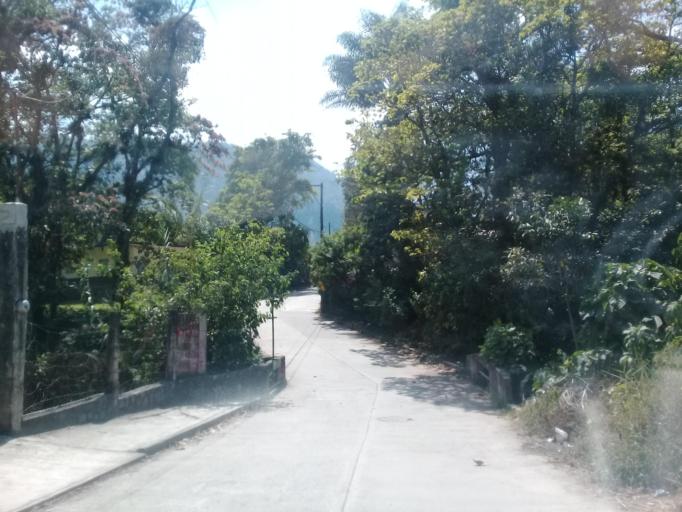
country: MX
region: Veracruz
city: Jalapilla
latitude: 18.8113
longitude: -97.0682
